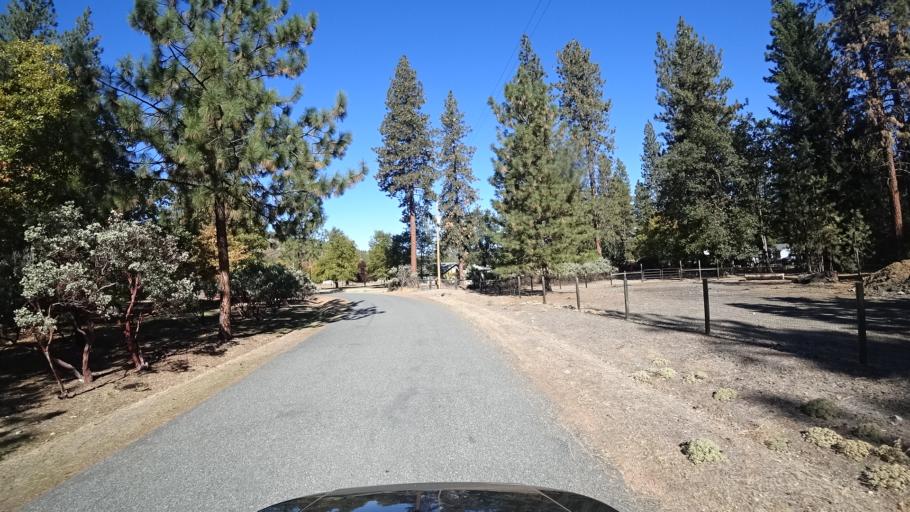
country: US
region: California
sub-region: Siskiyou County
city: Yreka
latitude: 41.5214
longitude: -122.9214
